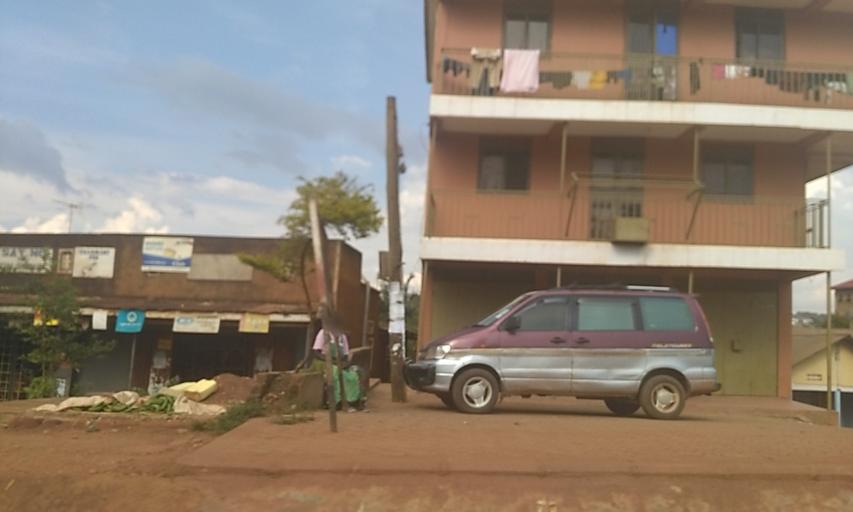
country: UG
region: Central Region
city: Kampala Central Division
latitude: 0.3338
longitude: 32.5493
